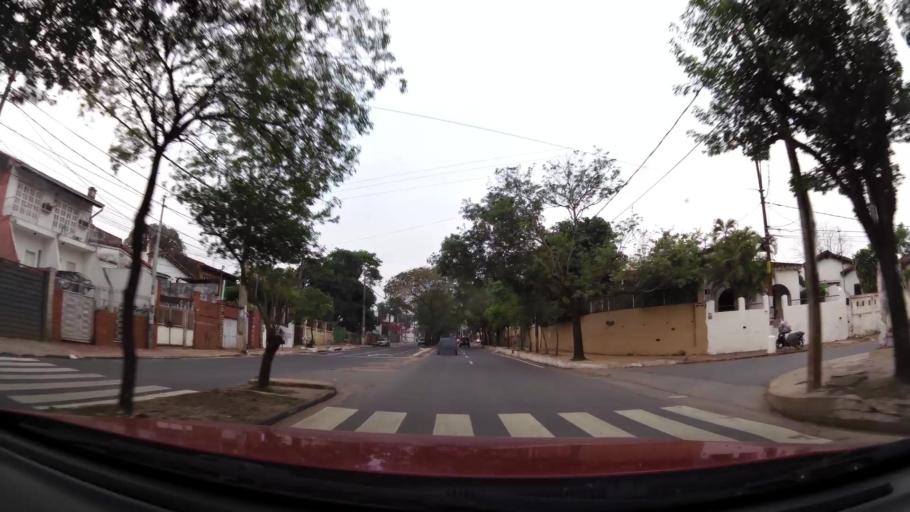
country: PY
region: Asuncion
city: Asuncion
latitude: -25.3107
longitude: -57.6167
